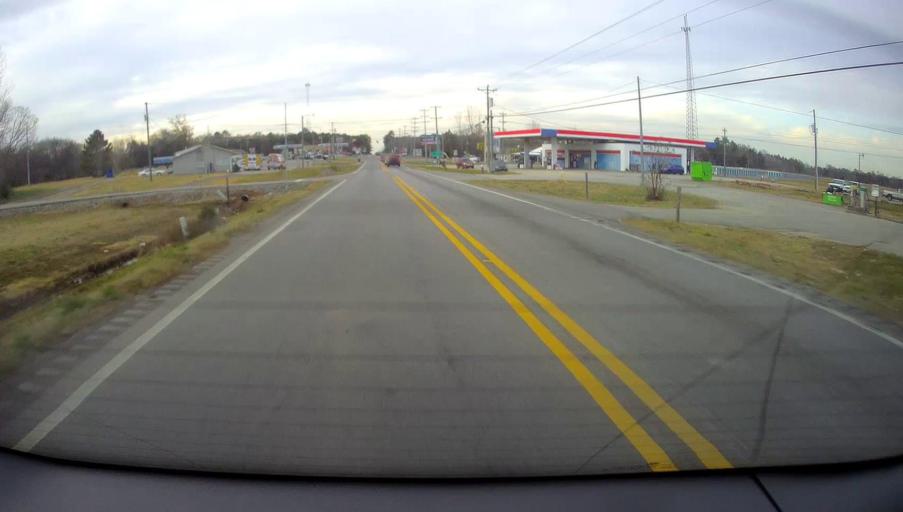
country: US
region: Alabama
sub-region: Morgan County
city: Priceville
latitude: 34.4451
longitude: -86.7546
